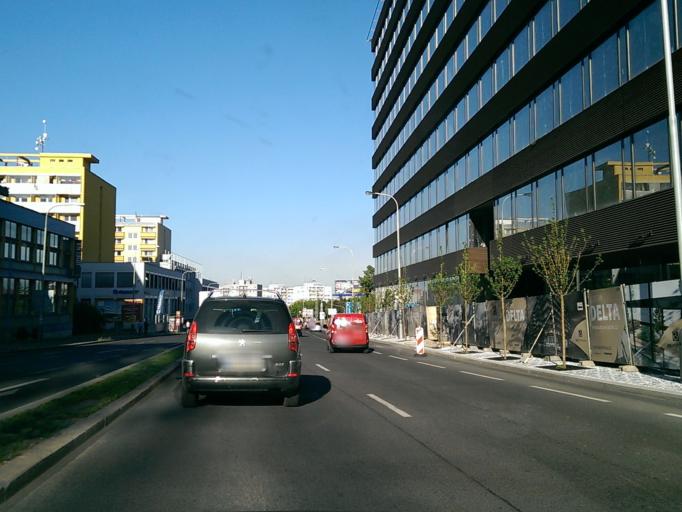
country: CZ
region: Praha
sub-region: Praha 2
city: Vysehrad
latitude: 50.0481
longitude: 14.4567
